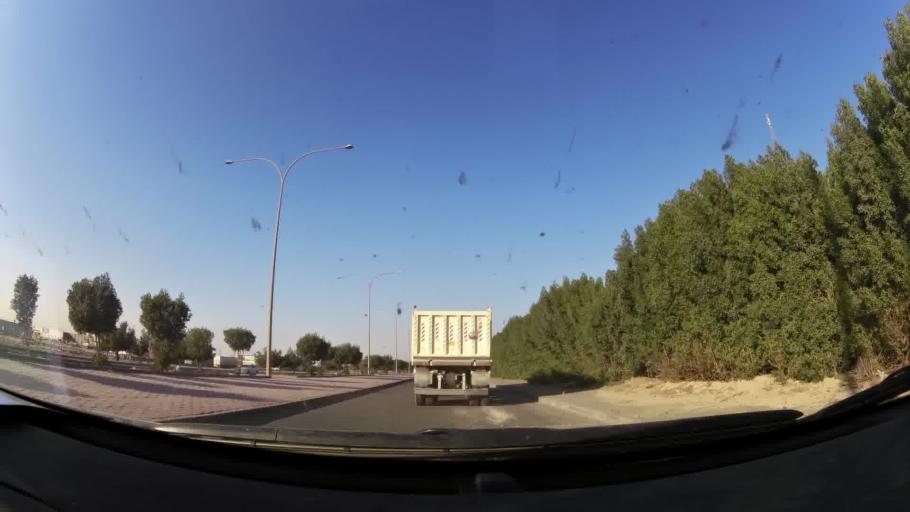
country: KW
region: Al Ahmadi
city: Al Fahahil
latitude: 28.9956
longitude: 48.1256
